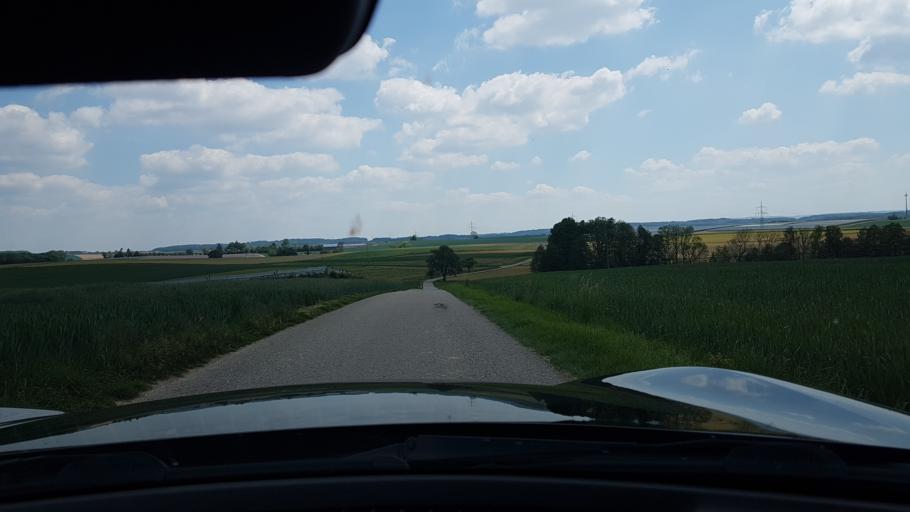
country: DE
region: Baden-Wuerttemberg
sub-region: Regierungsbezirk Stuttgart
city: Widdern
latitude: 49.2630
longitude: 9.4202
